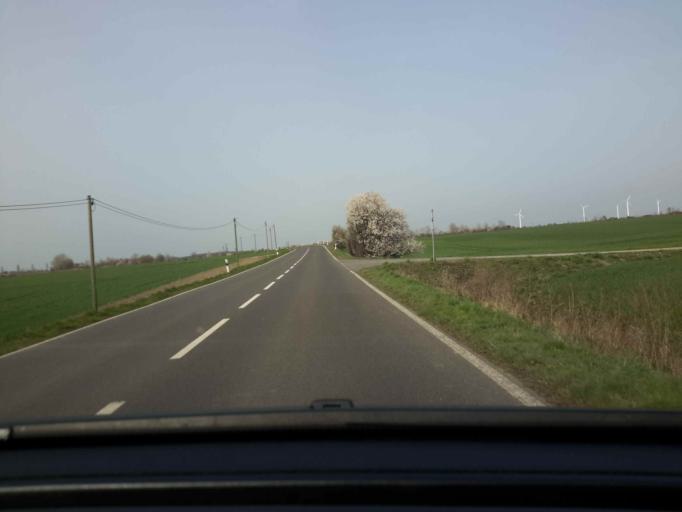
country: DE
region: Saxony
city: Rackwitz
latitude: 51.4412
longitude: 12.3539
